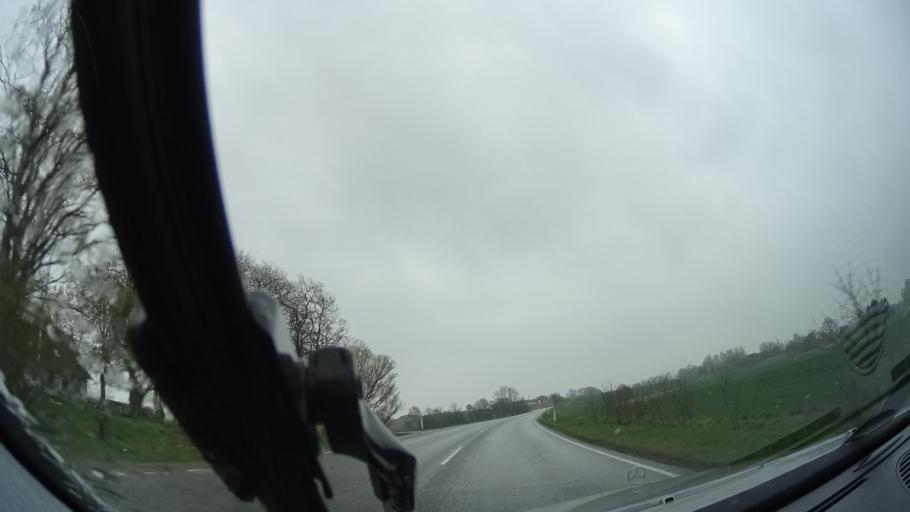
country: DK
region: Zealand
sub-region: Odsherred Kommune
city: Asnaes
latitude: 55.7978
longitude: 11.6028
